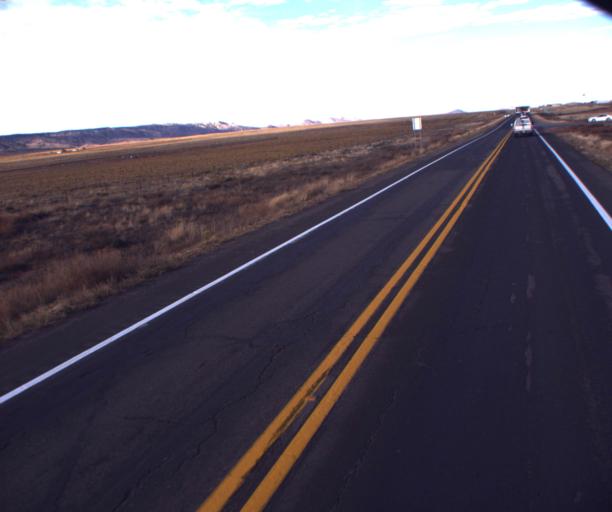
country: US
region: Arizona
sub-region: Apache County
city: Lukachukai
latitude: 36.9599
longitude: -109.3550
